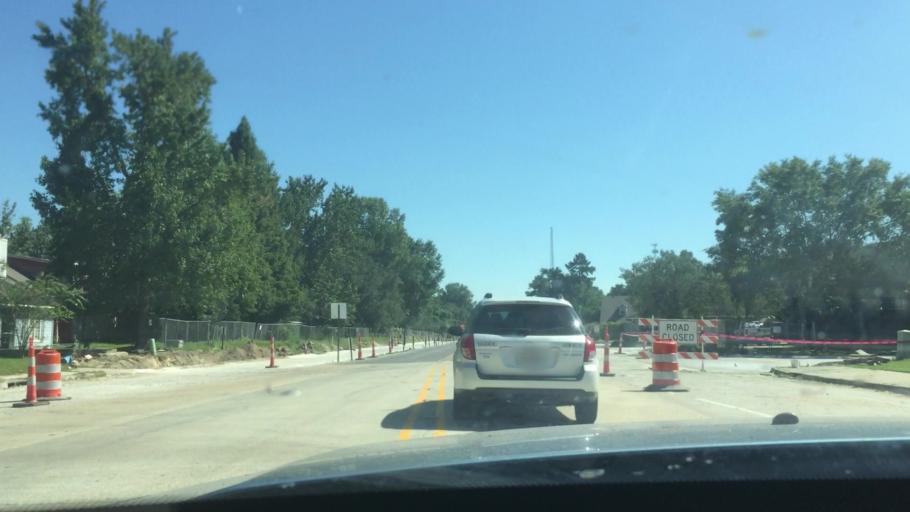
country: US
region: Louisiana
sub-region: East Baton Rouge Parish
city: Shenandoah
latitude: 30.4247
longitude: -91.0076
